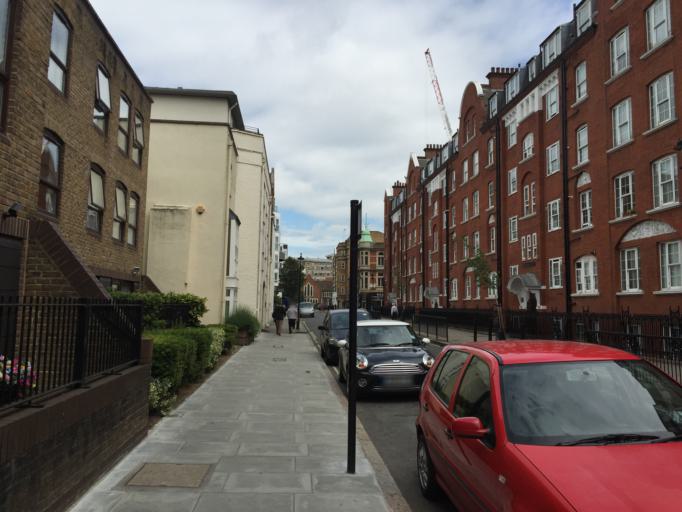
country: GB
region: England
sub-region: Greater London
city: London
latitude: 51.4931
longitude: -0.1323
